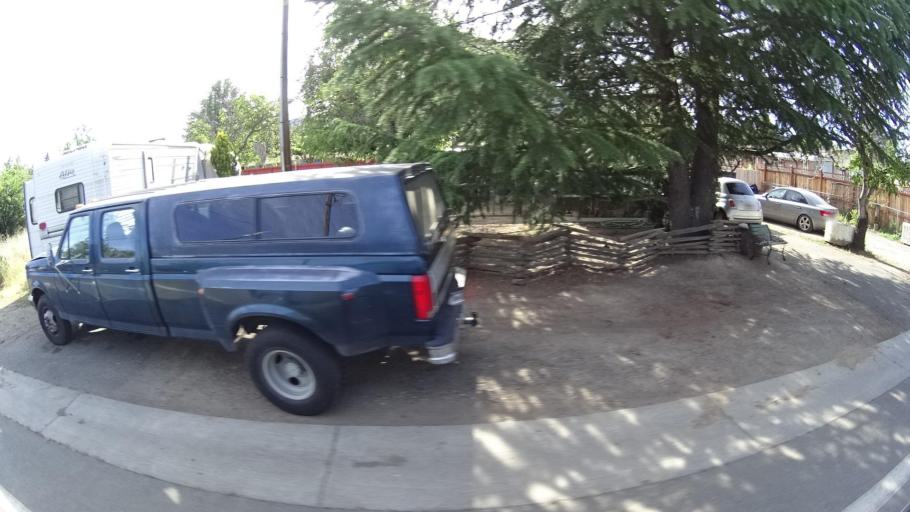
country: US
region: California
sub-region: Lake County
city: Kelseyville
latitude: 38.9808
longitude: -122.8315
